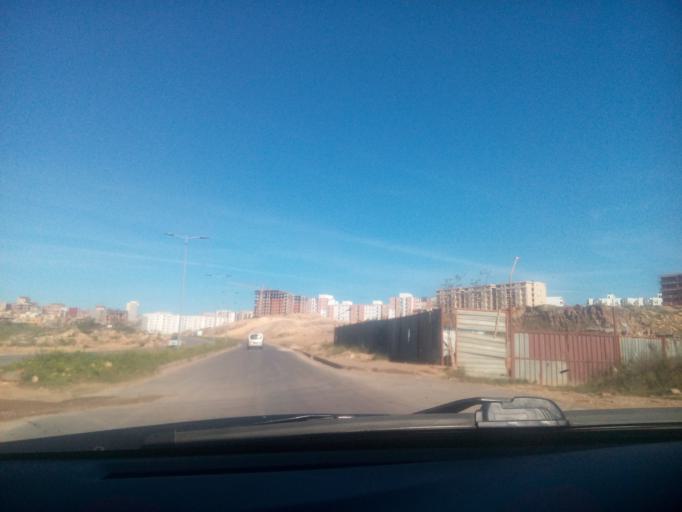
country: DZ
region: Oran
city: Bir el Djir
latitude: 35.7390
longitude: -0.5461
